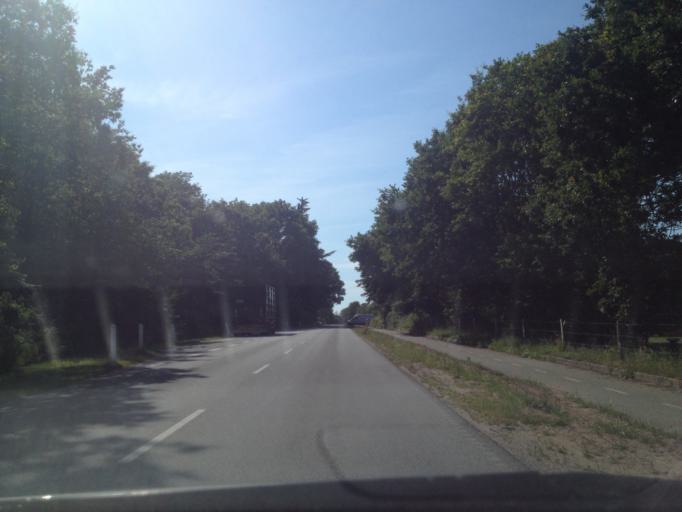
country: DK
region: Central Jutland
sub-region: Samso Kommune
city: Tranebjerg
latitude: 55.8614
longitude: 10.5589
